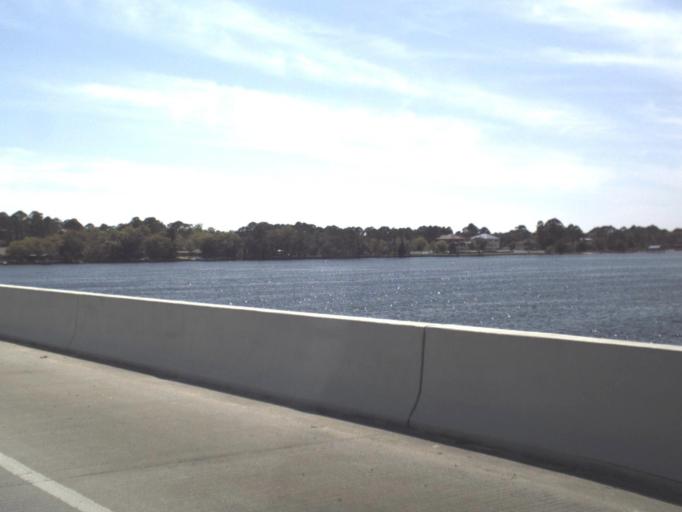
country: US
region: Florida
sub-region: Bay County
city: Lynn Haven
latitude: 30.2598
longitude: -85.6468
